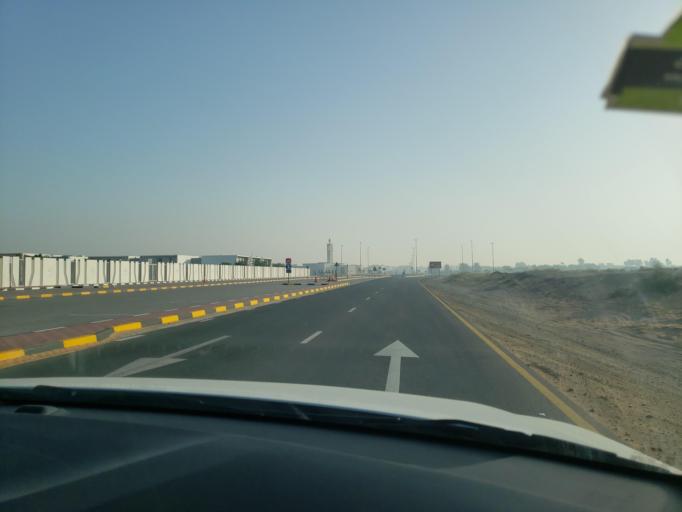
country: AE
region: Umm al Qaywayn
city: Umm al Qaywayn
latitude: 25.4673
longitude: 55.6124
